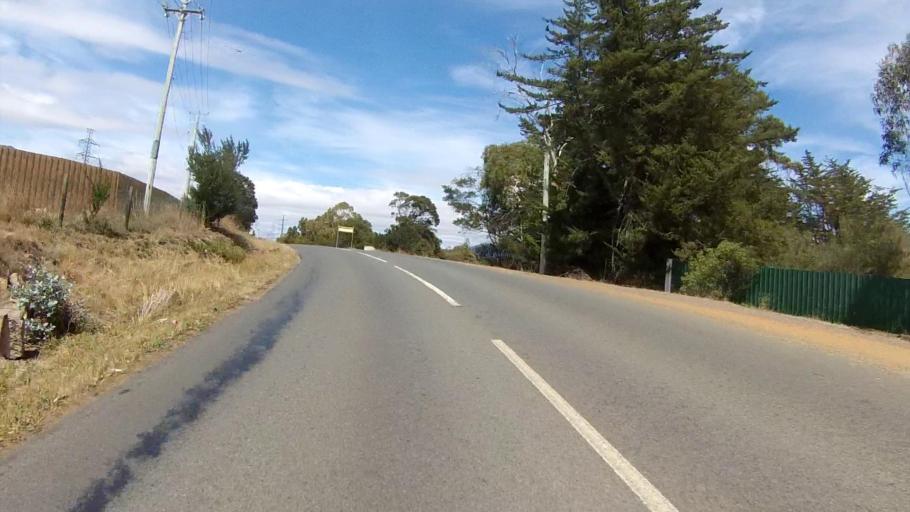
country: AU
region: Tasmania
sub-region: Clarence
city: Lindisfarne
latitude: -42.8215
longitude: 147.3499
